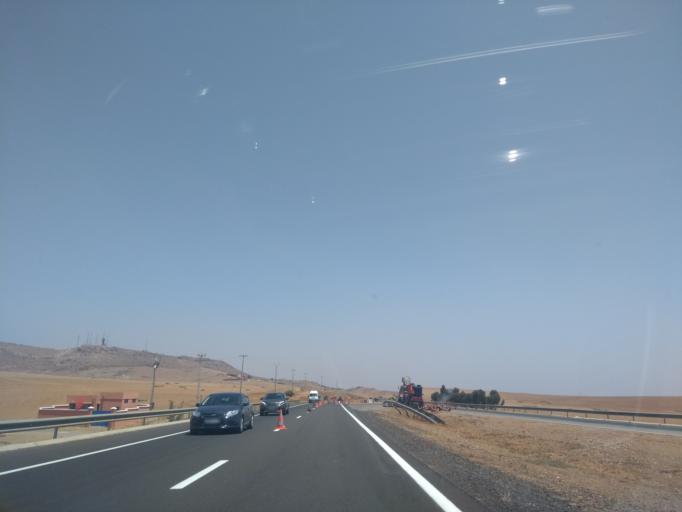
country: MA
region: Marrakech-Tensift-Al Haouz
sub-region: Kelaa-Des-Sraghna
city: Sidi Abdallah
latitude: 32.4547
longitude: -7.9312
